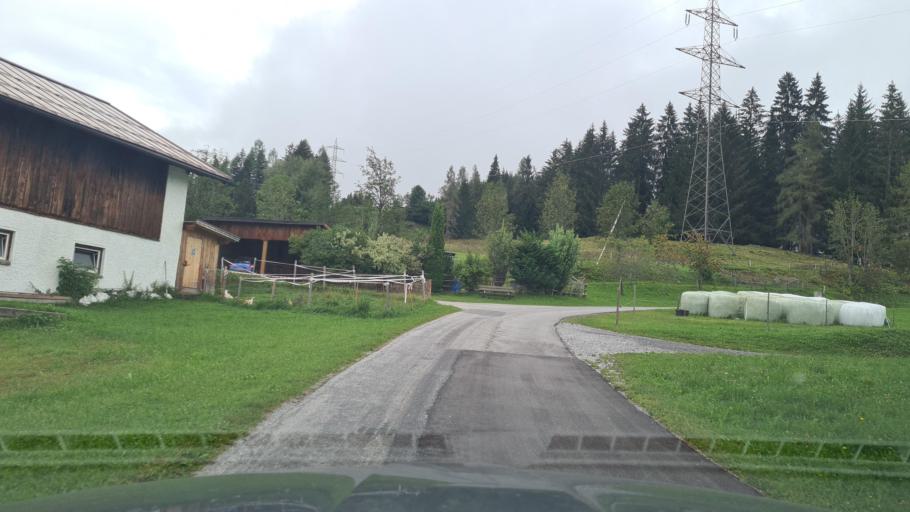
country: AT
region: Salzburg
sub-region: Politischer Bezirk Sankt Johann im Pongau
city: Sankt Johann im Pongau
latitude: 47.3564
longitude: 13.1802
